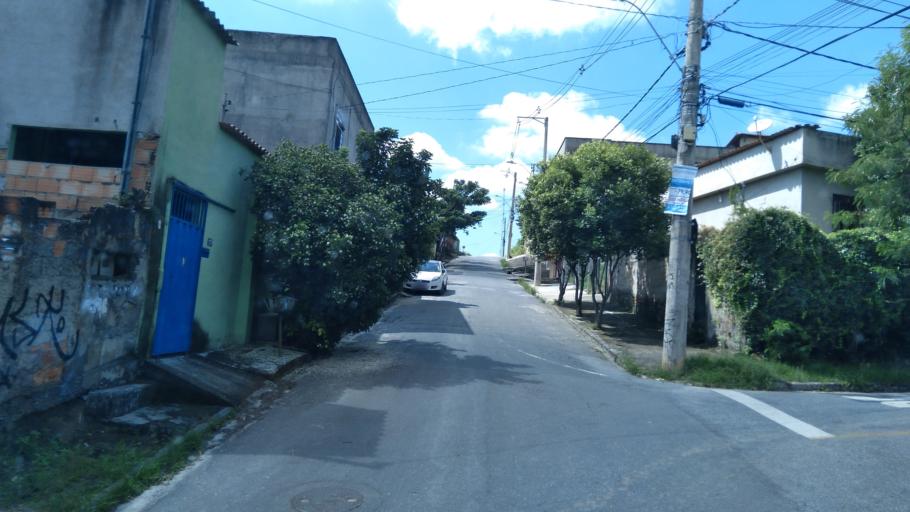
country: BR
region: Minas Gerais
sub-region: Santa Luzia
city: Santa Luzia
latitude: -19.8338
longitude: -43.8878
